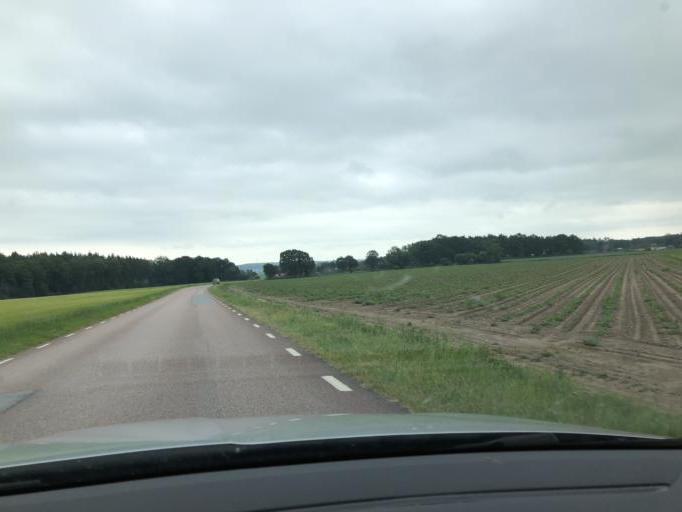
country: SE
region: Blekinge
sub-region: Solvesborgs Kommun
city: Soelvesborg
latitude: 56.1238
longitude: 14.6141
